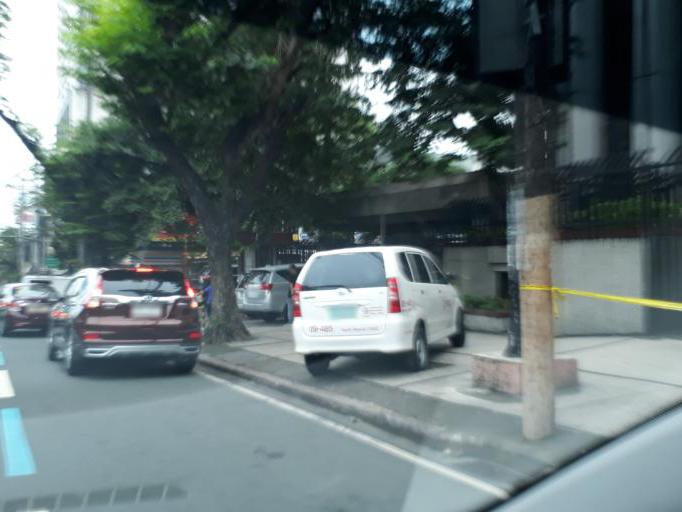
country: PH
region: Metro Manila
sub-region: City of Manila
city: Manila
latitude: 14.6172
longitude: 121.0009
